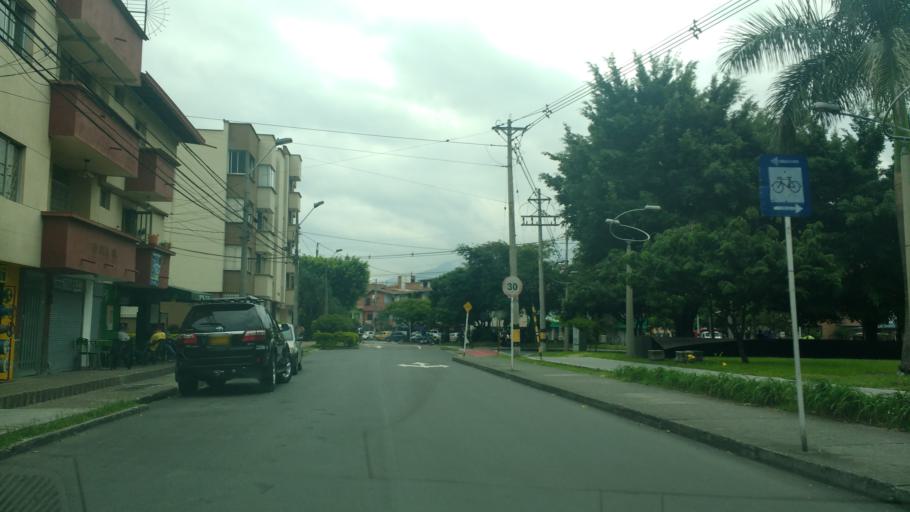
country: CO
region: Antioquia
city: Medellin
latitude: 6.2452
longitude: -75.5845
